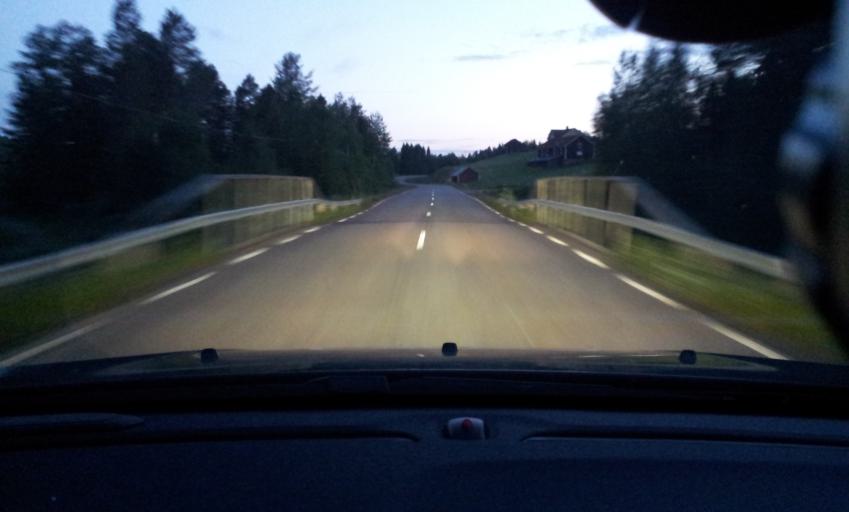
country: SE
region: Jaemtland
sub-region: OEstersunds Kommun
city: Brunflo
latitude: 62.6612
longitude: 14.8658
